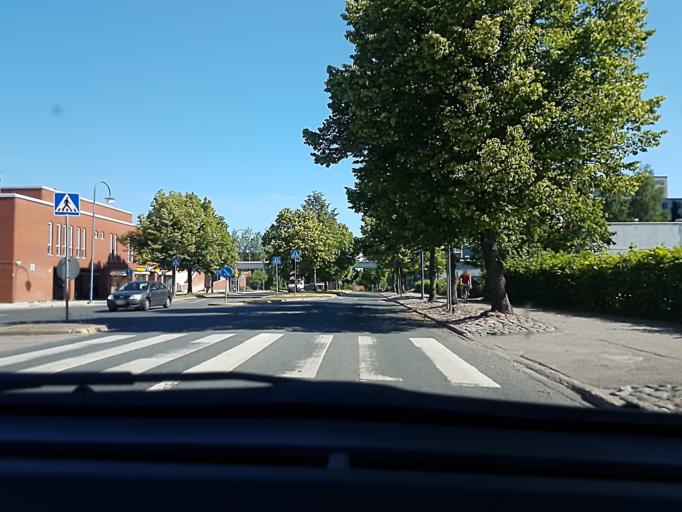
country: FI
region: Uusimaa
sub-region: Helsinki
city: Vantaa
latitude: 60.3224
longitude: 25.0626
